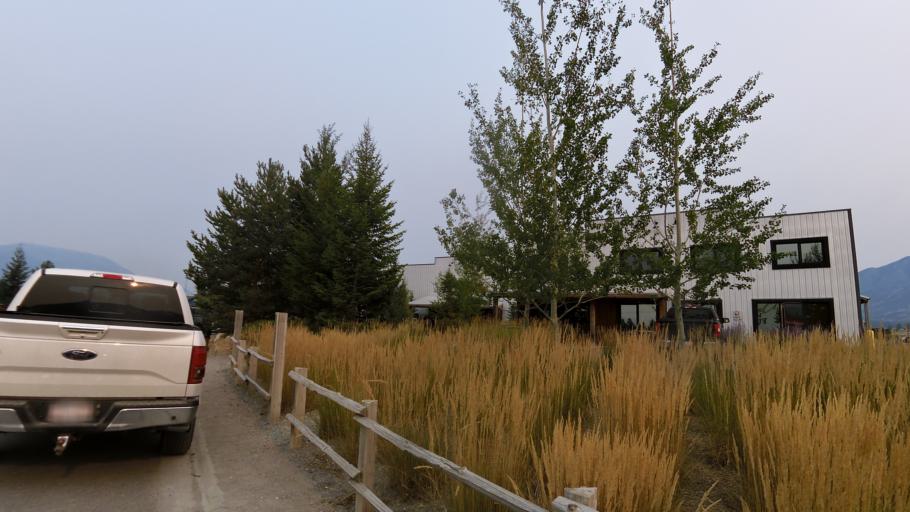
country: CA
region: British Columbia
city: Invermere
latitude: 50.5163
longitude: -116.0052
